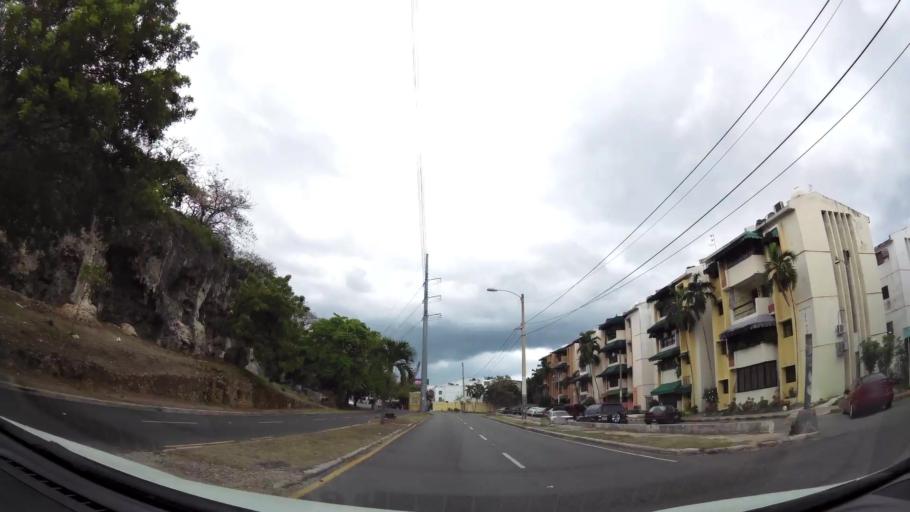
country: DO
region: Nacional
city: Bella Vista
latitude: 18.4439
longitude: -69.9470
